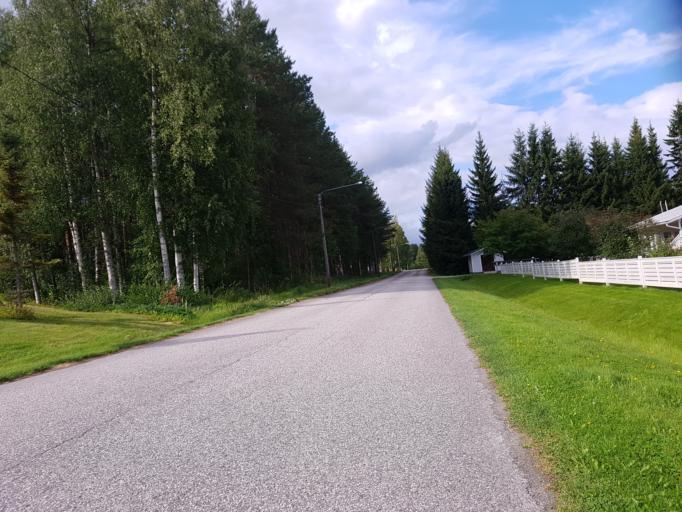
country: FI
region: Kainuu
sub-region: Kehys-Kainuu
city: Kuhmo
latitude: 64.1246
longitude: 29.5379
